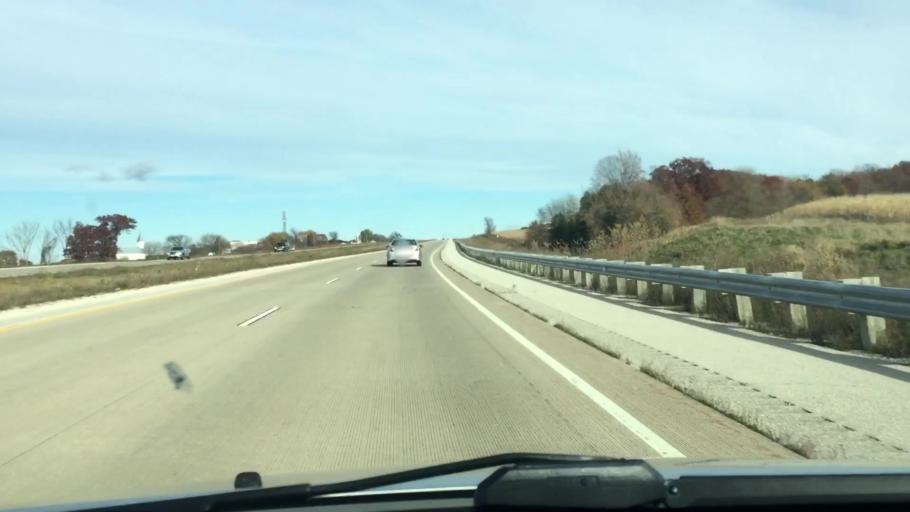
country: US
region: Wisconsin
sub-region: Kewaunee County
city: Luxemburg
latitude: 44.7075
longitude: -87.7011
